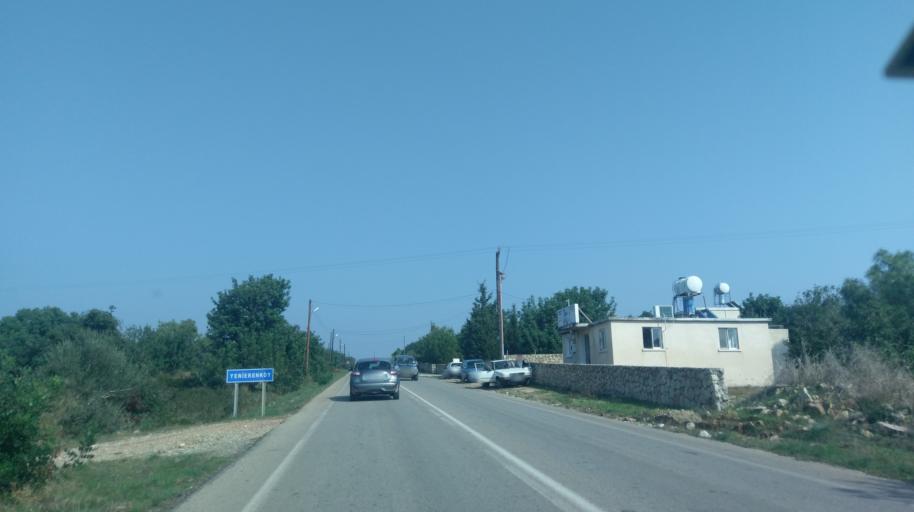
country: CY
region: Ammochostos
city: Leonarisso
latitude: 35.5220
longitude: 34.1746
